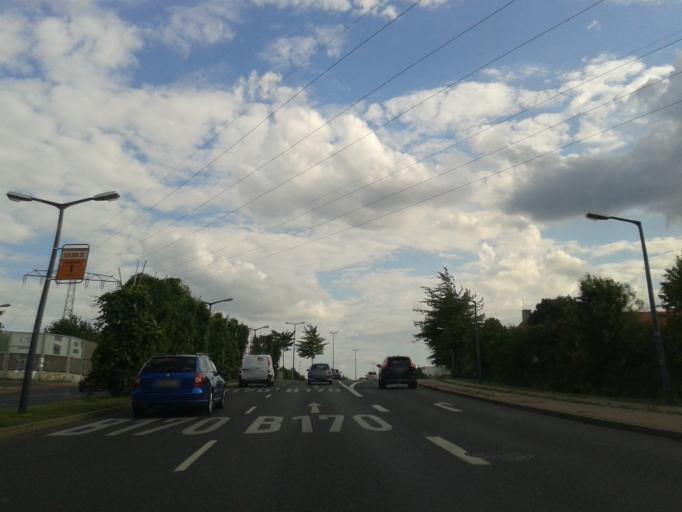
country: DE
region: Saxony
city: Dresden
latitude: 51.0226
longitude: 13.7303
